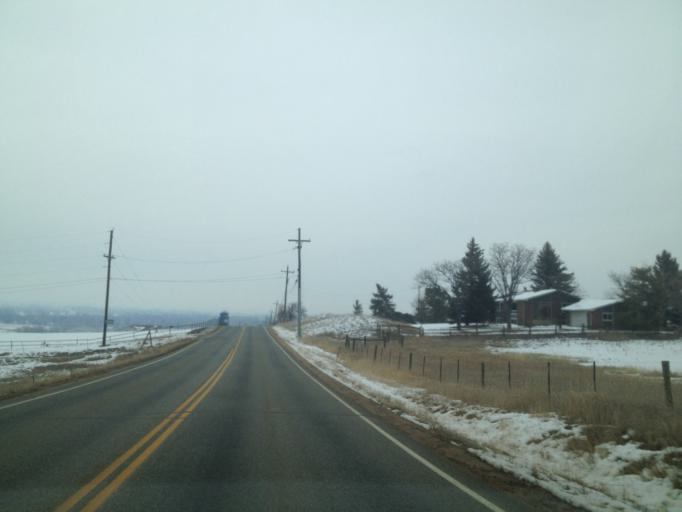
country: US
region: Colorado
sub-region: Boulder County
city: Gunbarrel
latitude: 40.0793
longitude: -105.1691
